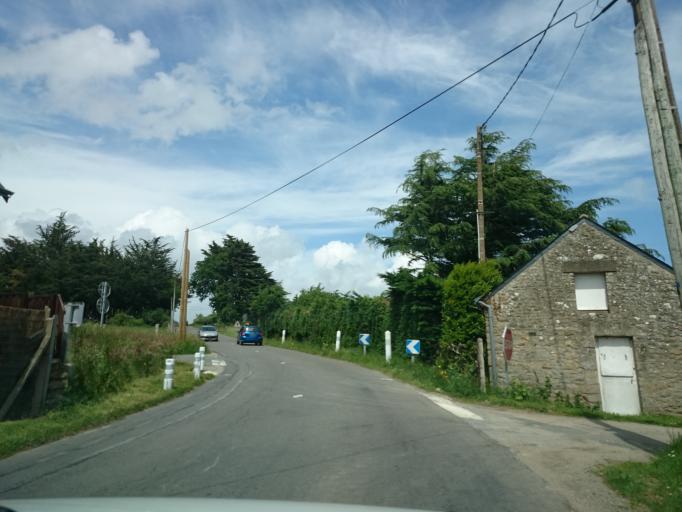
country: FR
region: Brittany
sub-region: Departement du Morbihan
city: Larmor-Baden
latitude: 47.6037
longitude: -2.8905
